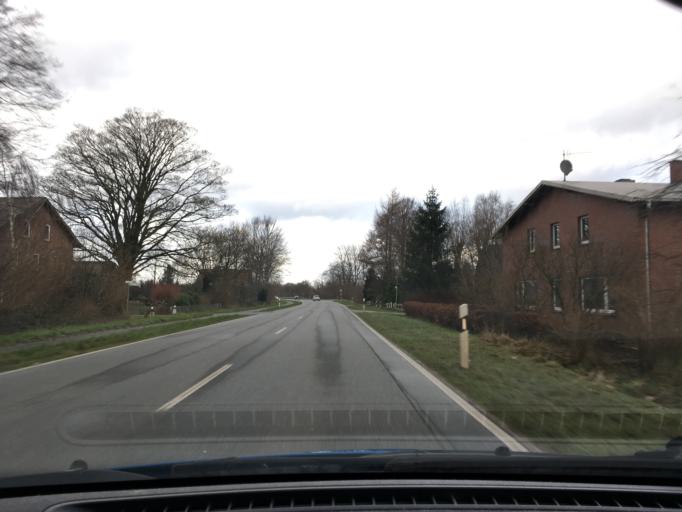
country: DE
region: Schleswig-Holstein
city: Kaisborstel
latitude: 54.0132
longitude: 9.4813
